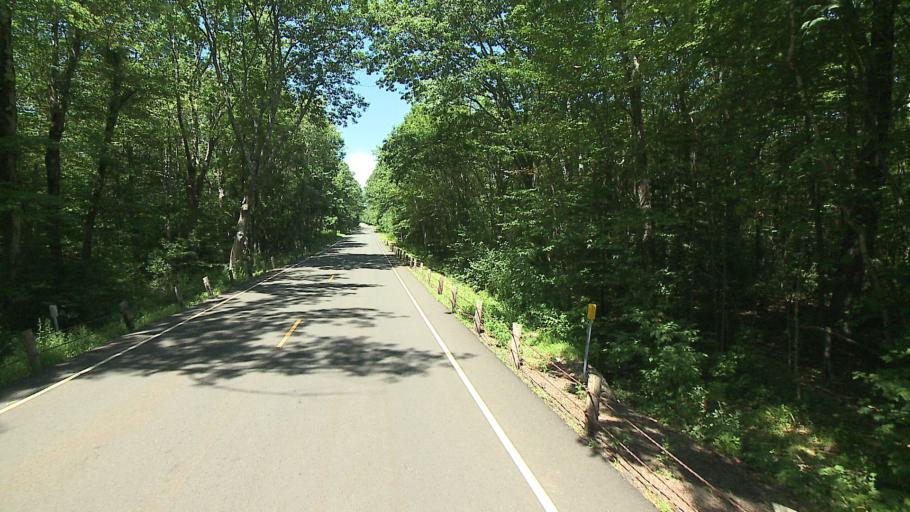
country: US
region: Connecticut
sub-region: Litchfield County
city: New Hartford Center
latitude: 41.9719
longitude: -72.9803
